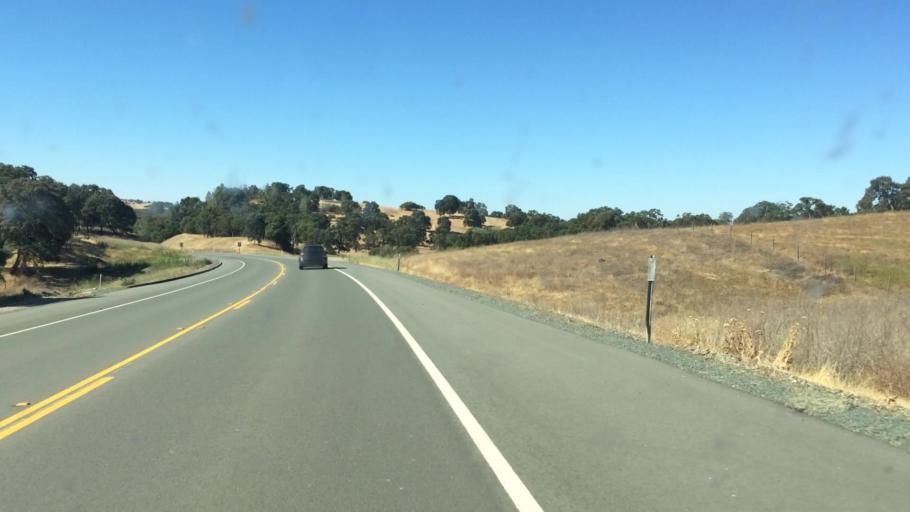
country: US
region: California
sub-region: Amador County
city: Plymouth
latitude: 38.4386
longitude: -120.8771
